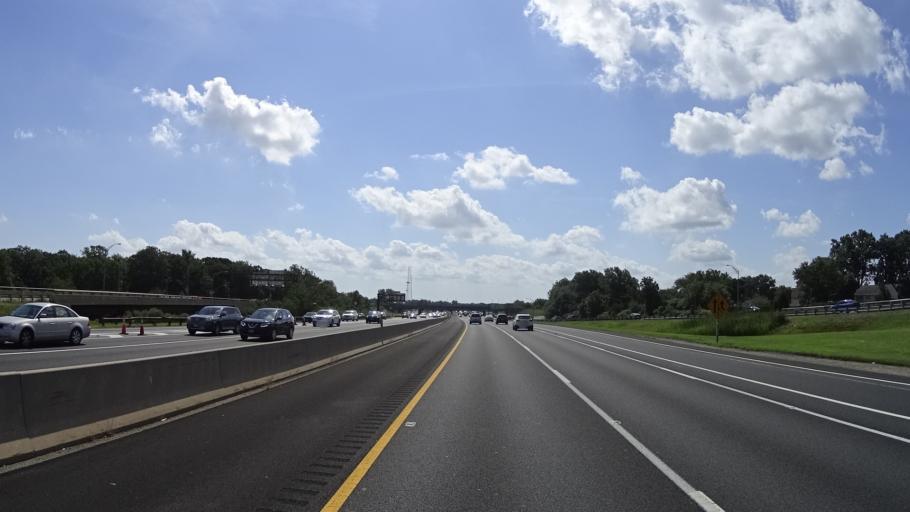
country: US
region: New Jersey
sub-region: Middlesex County
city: Fords
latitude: 40.5378
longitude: -74.3058
